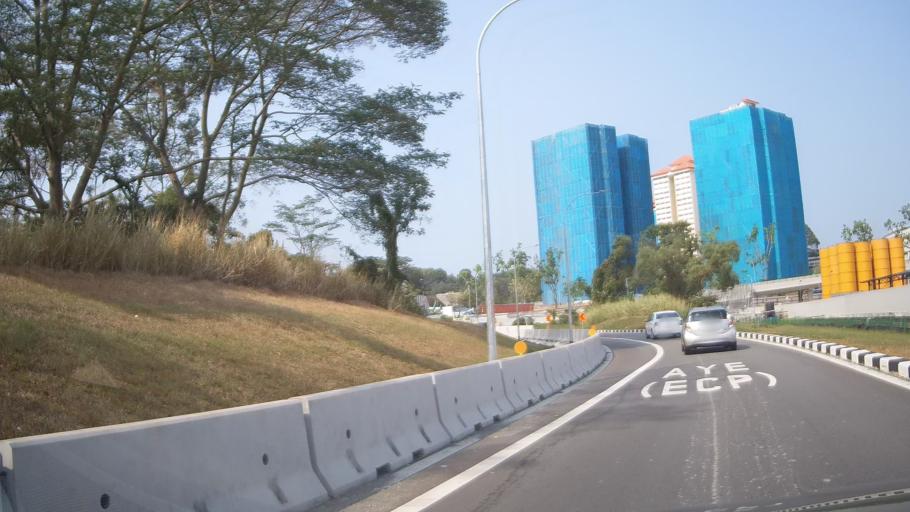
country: SG
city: Singapore
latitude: 1.2894
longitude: 103.7954
